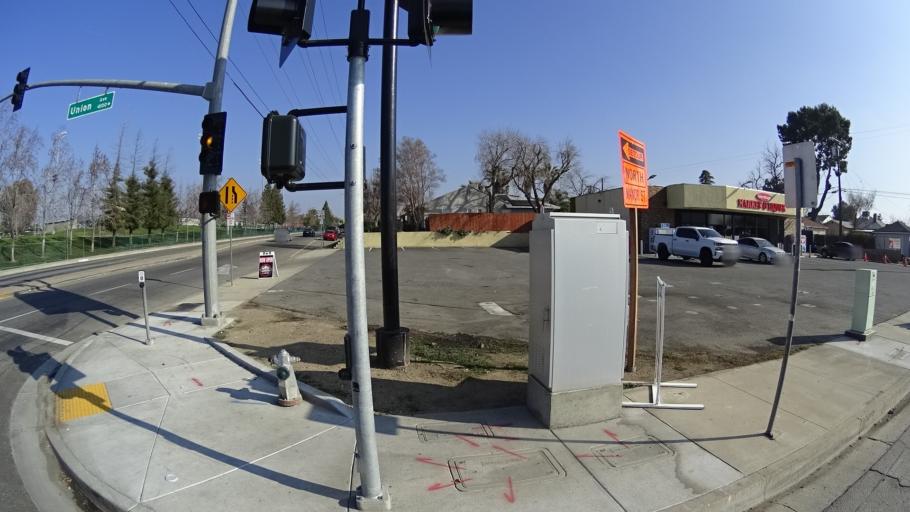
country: US
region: California
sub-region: Kern County
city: Oildale
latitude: 35.3973
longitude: -119.0028
